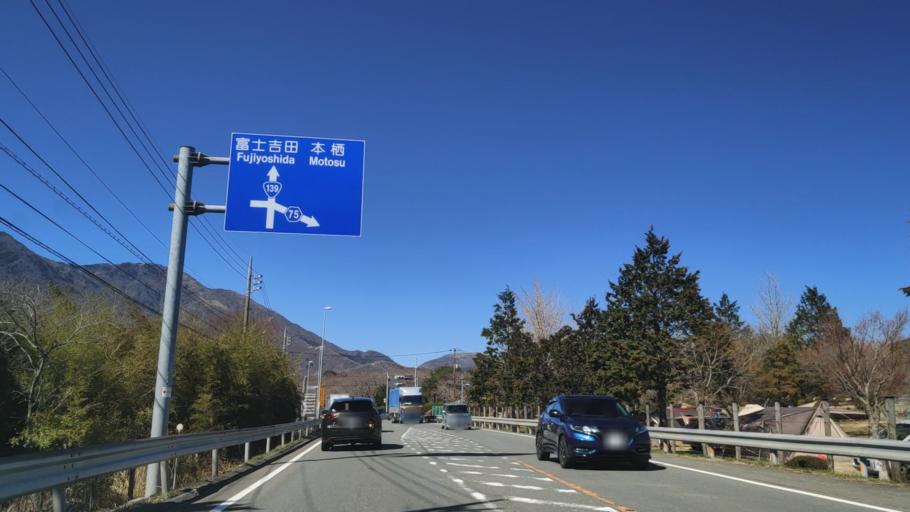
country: JP
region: Yamanashi
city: Fujikawaguchiko
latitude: 35.3736
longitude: 138.5759
